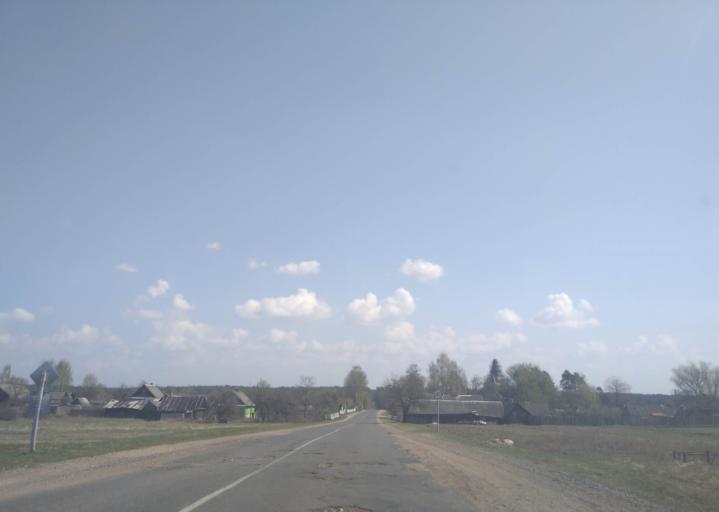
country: BY
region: Minsk
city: Loshnitsa
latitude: 54.4909
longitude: 28.6649
